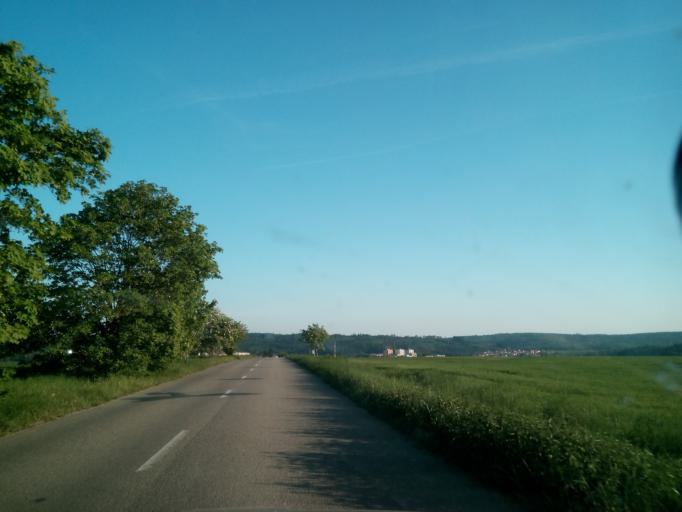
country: CZ
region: South Moravian
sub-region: Okres Blansko
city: Jedovnice
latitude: 49.3562
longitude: 16.7555
